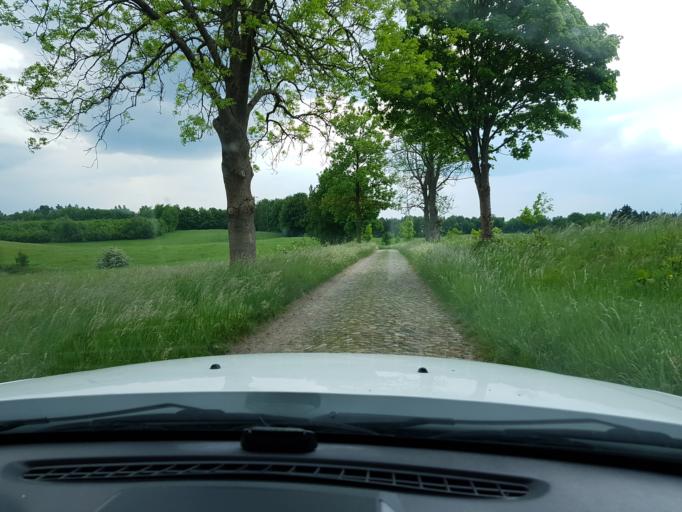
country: PL
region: West Pomeranian Voivodeship
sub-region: Powiat drawski
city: Drawsko Pomorskie
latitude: 53.5502
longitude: 15.7250
